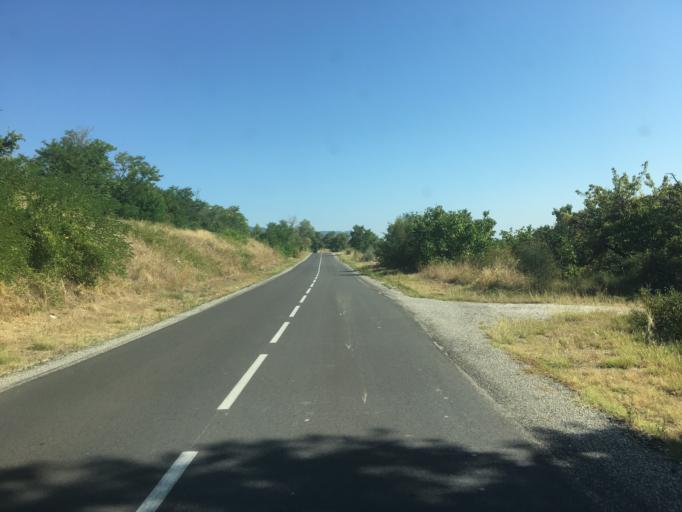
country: FR
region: Provence-Alpes-Cote d'Azur
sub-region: Departement des Alpes-de-Haute-Provence
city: Manosque
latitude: 43.8038
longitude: 5.7878
